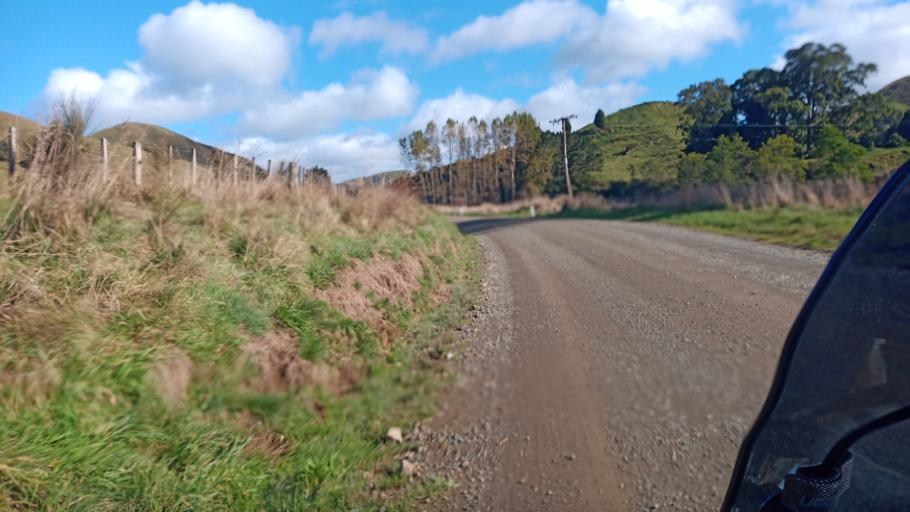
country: NZ
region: Bay of Plenty
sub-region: Opotiki District
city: Opotiki
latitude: -38.4632
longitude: 177.4258
